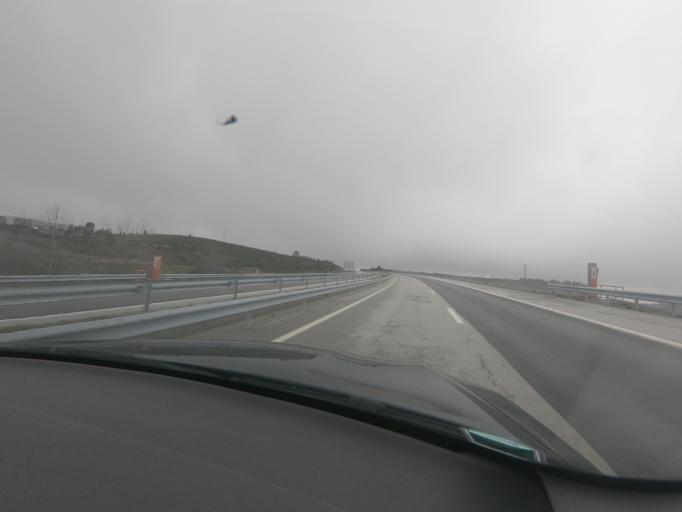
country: PT
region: Viseu
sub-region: Castro Daire
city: Castro Daire
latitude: 40.9453
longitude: -7.9027
